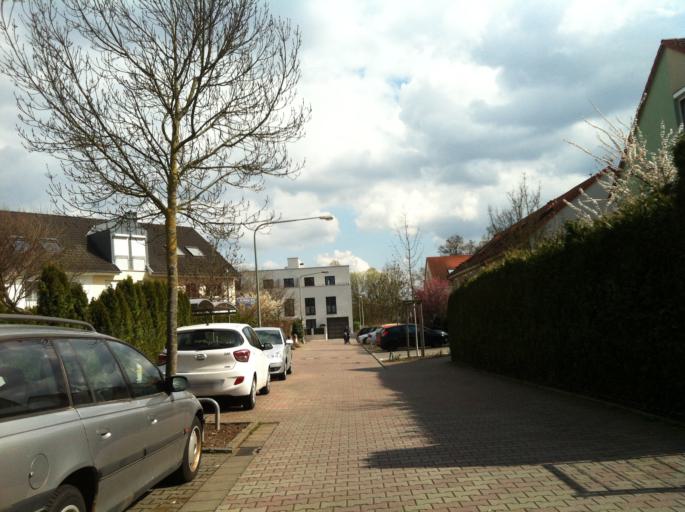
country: DE
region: Hesse
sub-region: Regierungsbezirk Darmstadt
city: Bad Homburg vor der Hoehe
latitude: 50.1676
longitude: 8.6392
